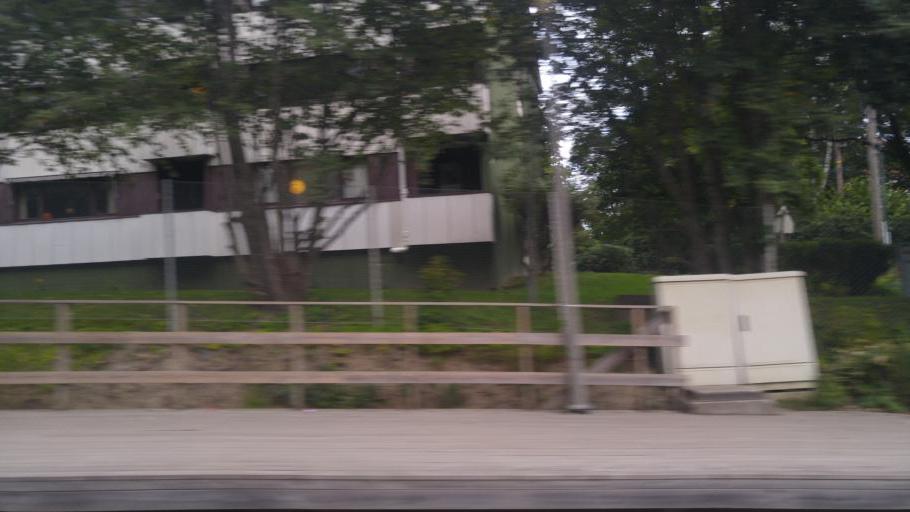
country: NO
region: Oslo
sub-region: Oslo
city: Sjolyststranda
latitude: 59.9511
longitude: 10.6942
